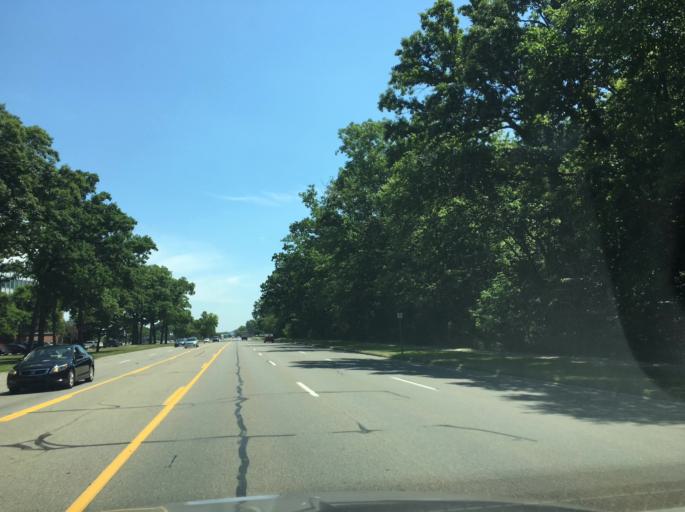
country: US
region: Michigan
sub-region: Wayne County
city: Allen Park
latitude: 42.2934
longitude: -83.2259
